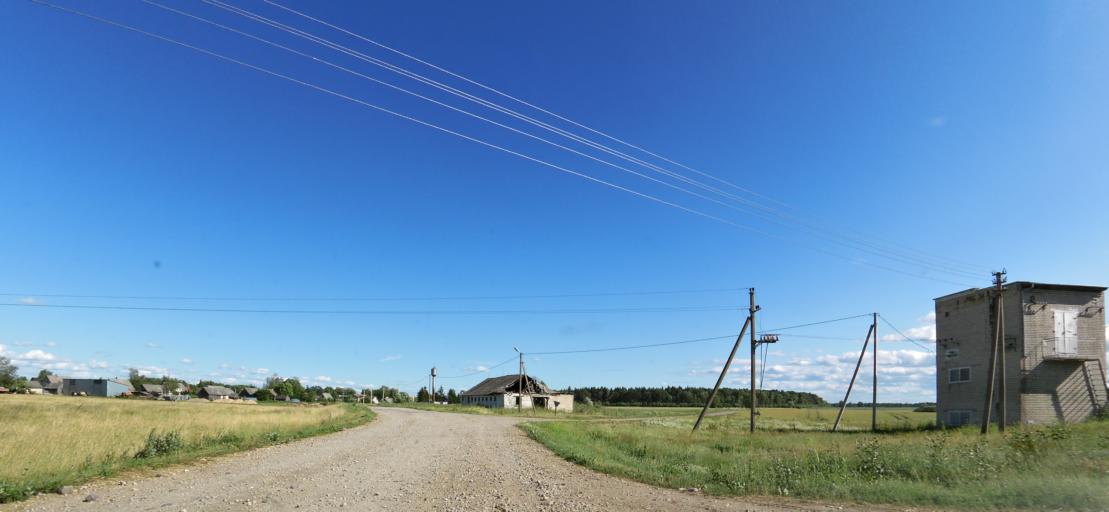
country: LT
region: Panevezys
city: Pasvalys
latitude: 56.1603
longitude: 24.4351
